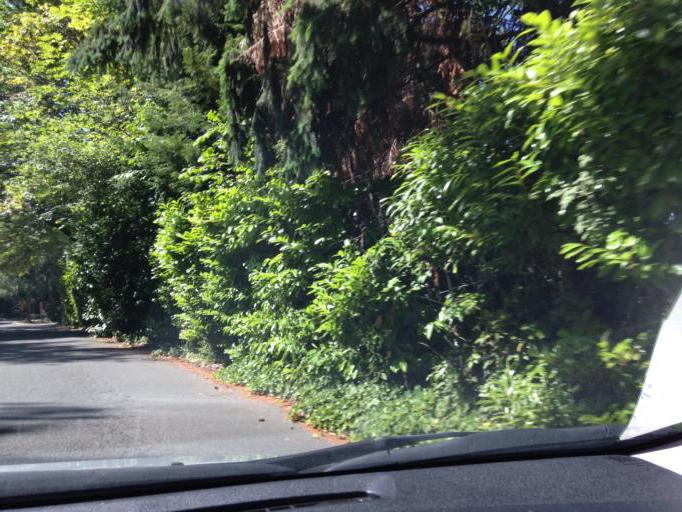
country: US
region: Washington
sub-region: King County
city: Seattle
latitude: 47.6210
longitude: -122.2823
